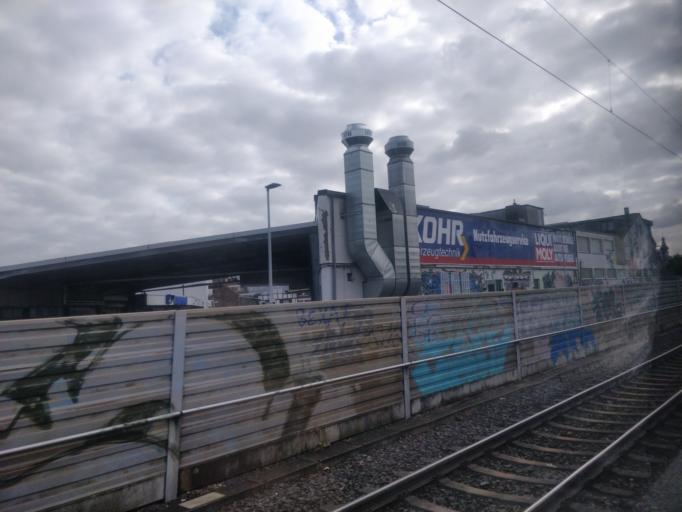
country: DE
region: North Rhine-Westphalia
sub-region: Regierungsbezirk Koln
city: Siegburg
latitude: 50.7961
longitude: 7.1996
